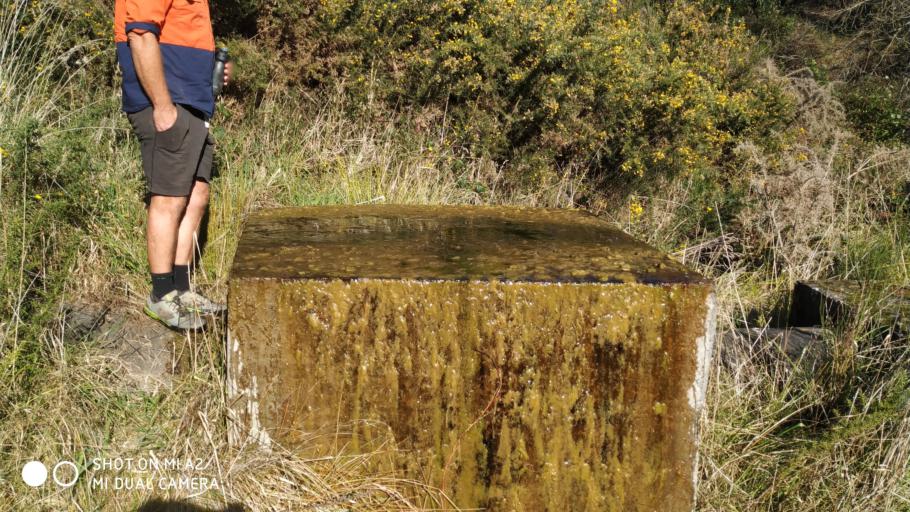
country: NZ
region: Nelson
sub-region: Nelson City
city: Nelson
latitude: -41.2927
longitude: 173.3158
